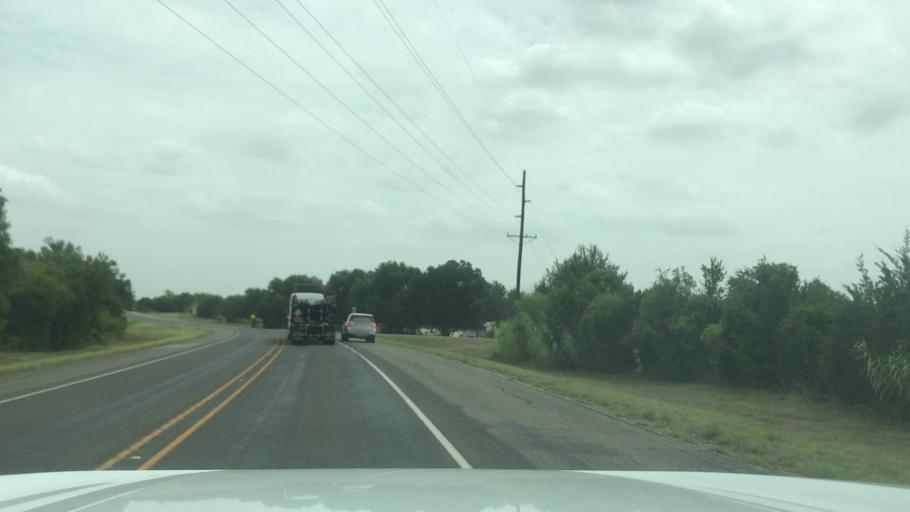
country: US
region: Texas
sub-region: Bosque County
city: Valley Mills
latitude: 31.6757
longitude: -97.5201
